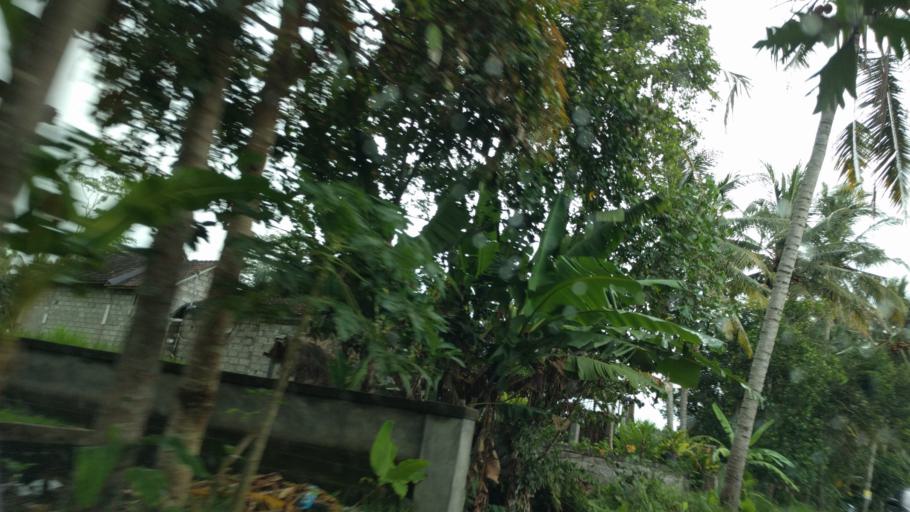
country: ID
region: Bali
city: Banjar Triwangsakeliki
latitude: -8.4607
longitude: 115.2594
